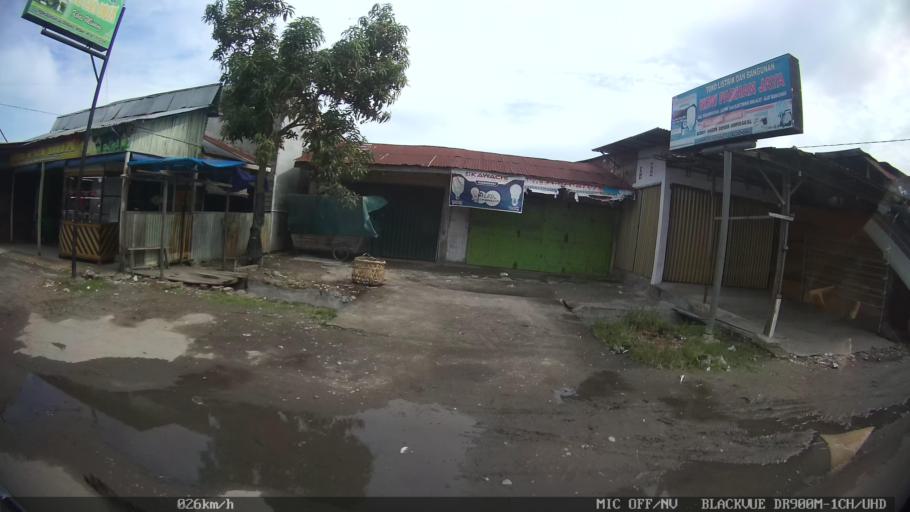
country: ID
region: North Sumatra
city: Medan
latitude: 3.6209
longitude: 98.7303
